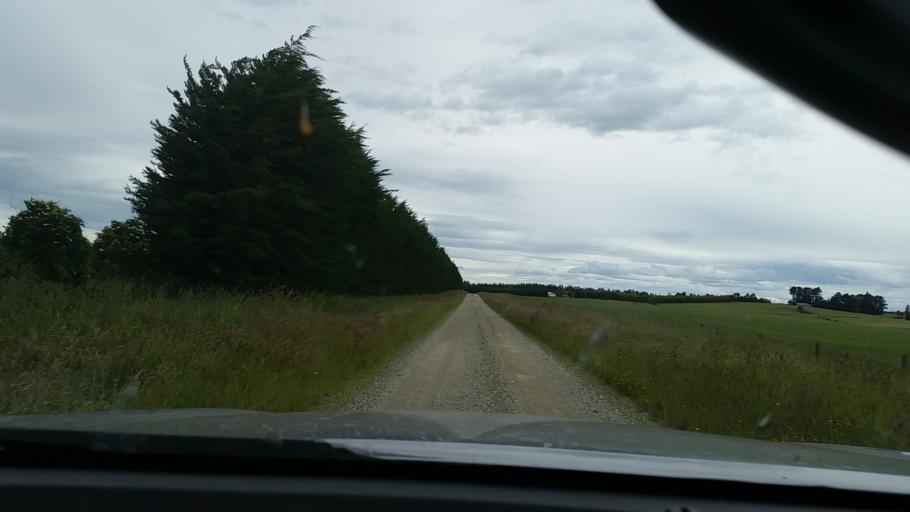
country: NZ
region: Southland
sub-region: Invercargill City
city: Invercargill
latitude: -46.2705
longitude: 168.5398
